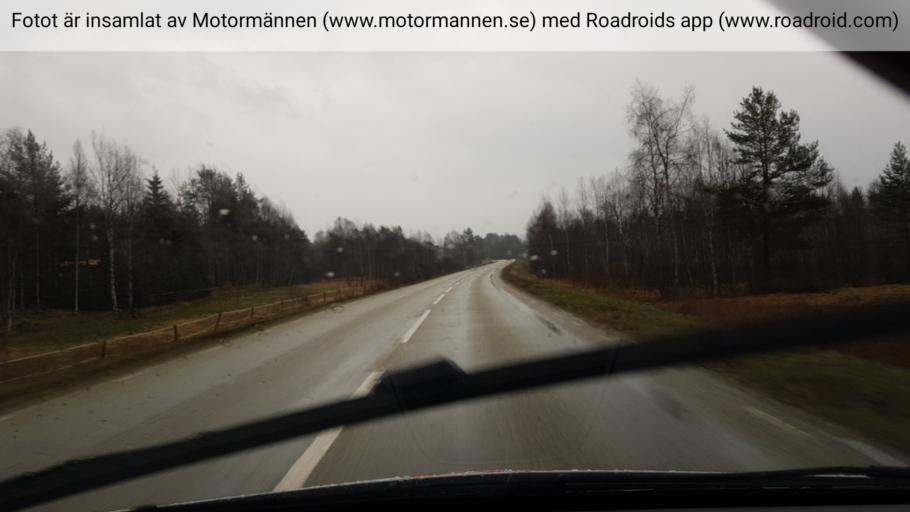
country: SE
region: Jaemtland
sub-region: Harjedalens Kommun
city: Sveg
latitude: 62.4111
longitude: 13.6814
